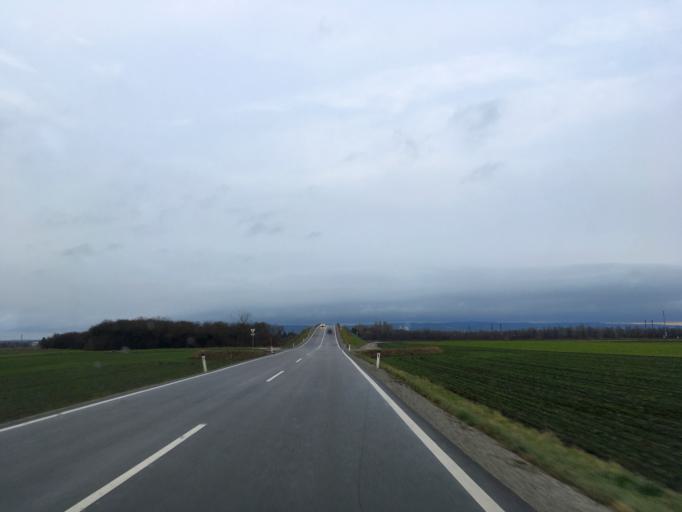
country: AT
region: Lower Austria
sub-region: Politischer Bezirk Bruck an der Leitha
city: Gotzendorf an der Leitha
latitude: 48.0288
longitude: 16.5633
